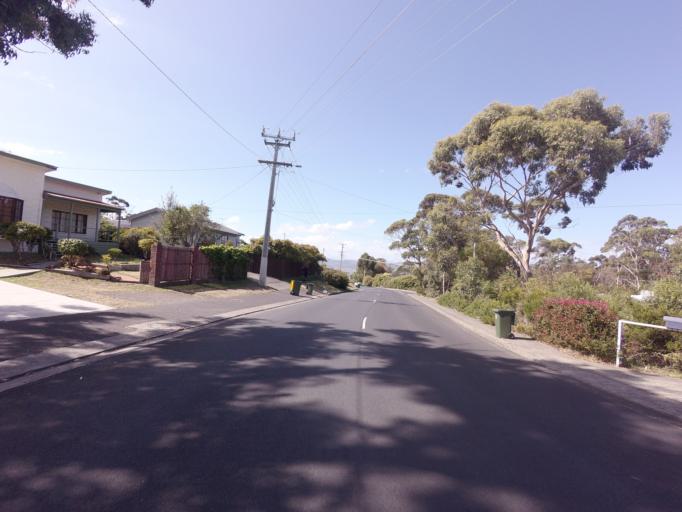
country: AU
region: Tasmania
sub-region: Hobart
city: Dynnyrne
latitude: -42.9198
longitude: 147.3231
